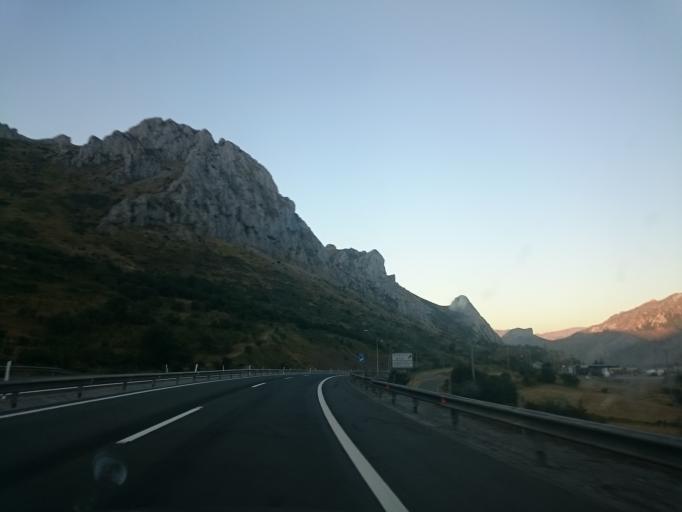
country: ES
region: Castille and Leon
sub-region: Provincia de Leon
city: Sena de Luna
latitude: 42.9303
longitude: -5.8526
